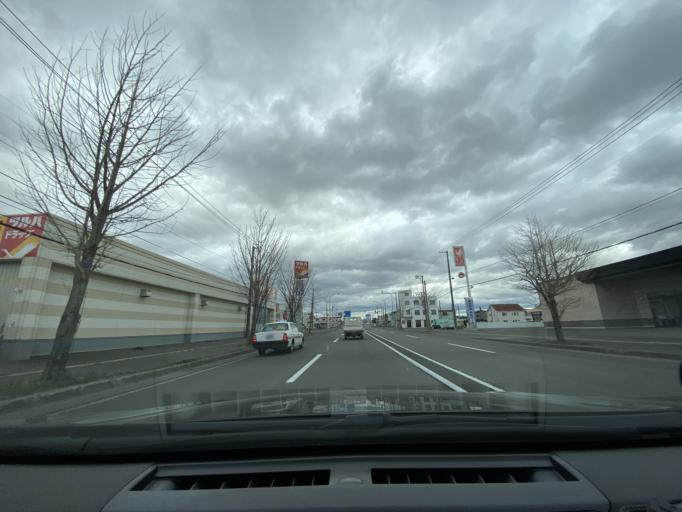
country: JP
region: Hokkaido
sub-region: Asahikawa-shi
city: Asahikawa
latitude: 43.8121
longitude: 142.3983
